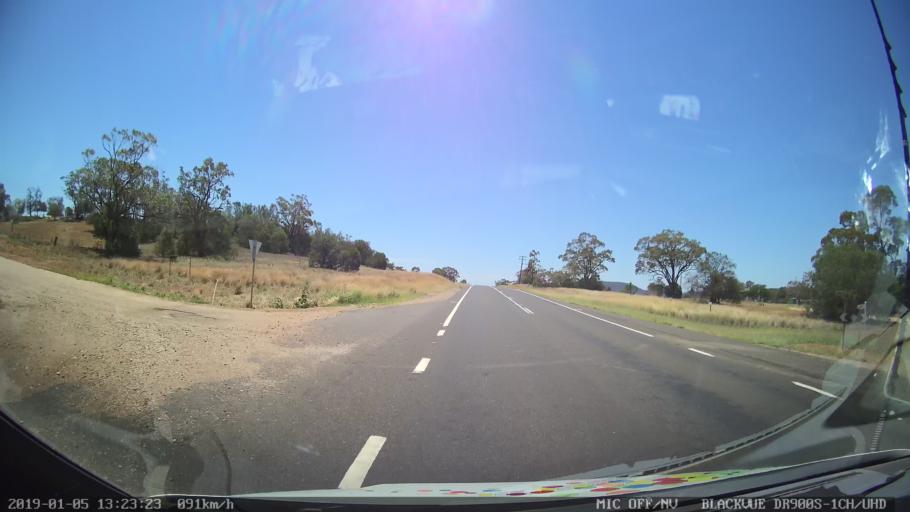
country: AU
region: New South Wales
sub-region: Gunnedah
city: Gunnedah
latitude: -31.0784
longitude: 149.9746
